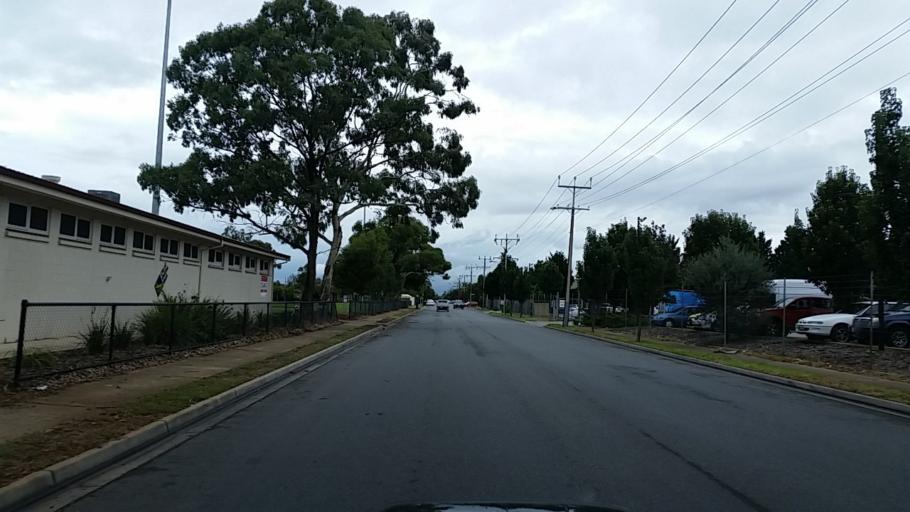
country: AU
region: South Australia
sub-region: Charles Sturt
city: Findon
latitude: -34.8973
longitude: 138.5415
